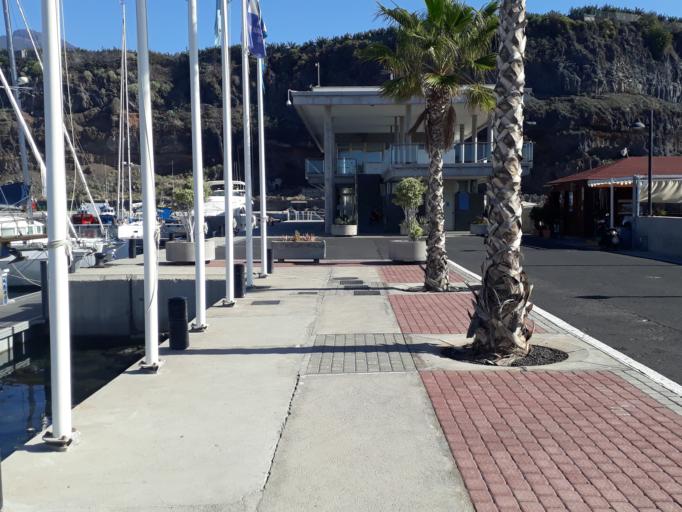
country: ES
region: Canary Islands
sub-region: Provincia de Santa Cruz de Tenerife
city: Tazacorte
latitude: 28.6435
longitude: -17.9435
